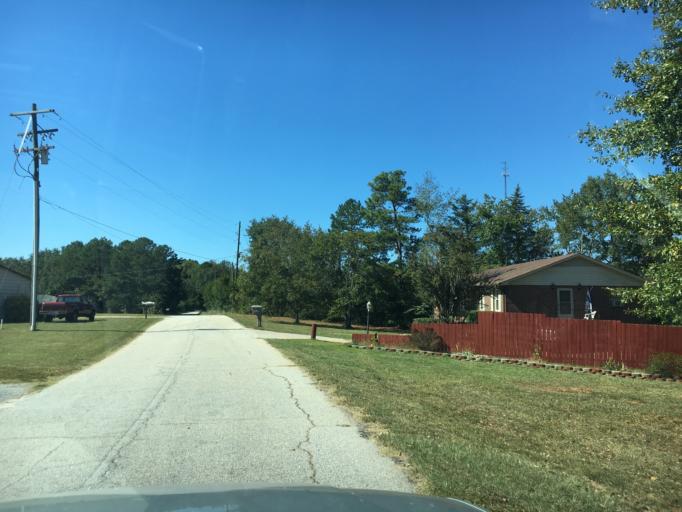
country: US
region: South Carolina
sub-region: Oconee County
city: Utica
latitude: 34.7063
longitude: -82.9218
